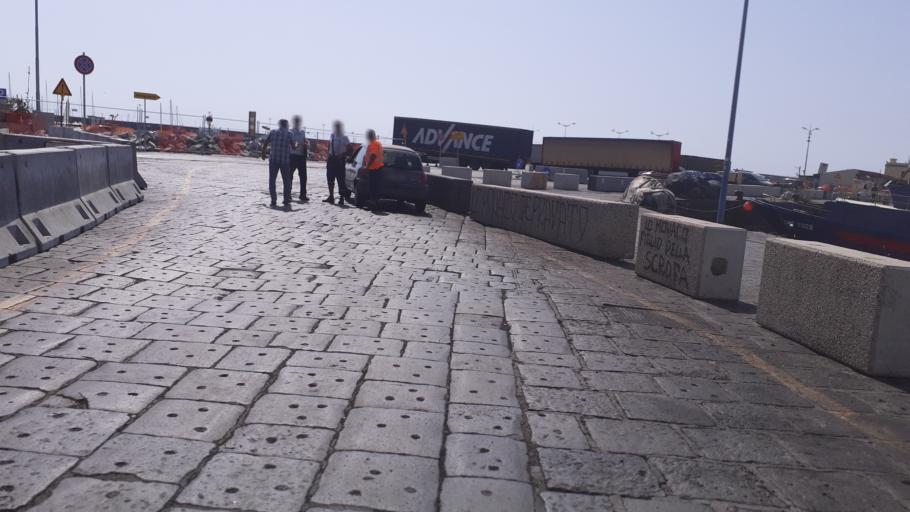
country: IT
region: Sicily
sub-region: Catania
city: Catania
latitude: 37.5002
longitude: 15.0941
